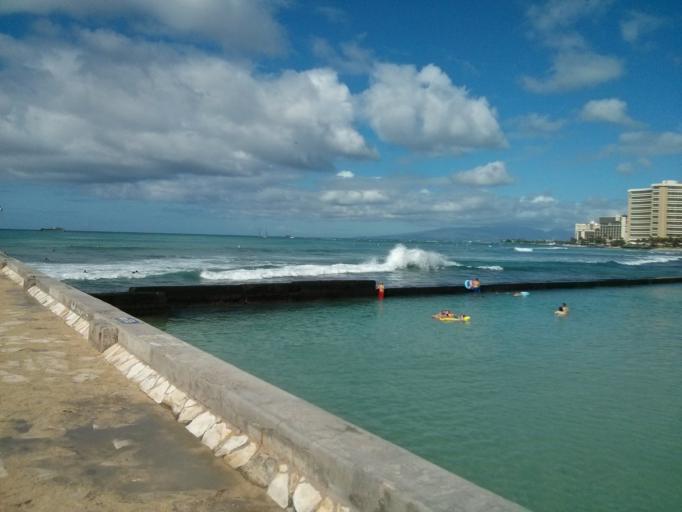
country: US
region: Hawaii
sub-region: Honolulu County
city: Honolulu
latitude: 21.2713
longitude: -157.8233
